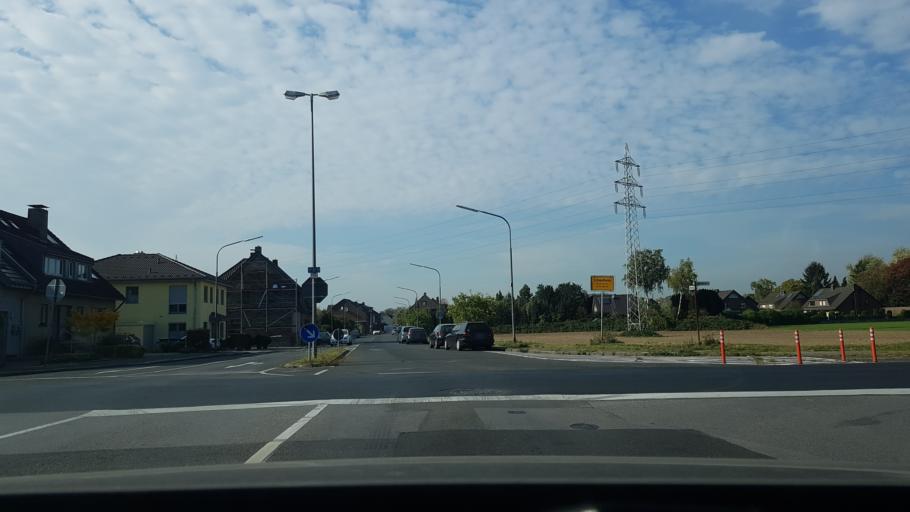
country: DE
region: North Rhine-Westphalia
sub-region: Regierungsbezirk Dusseldorf
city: Moers
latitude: 51.4196
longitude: 6.6650
